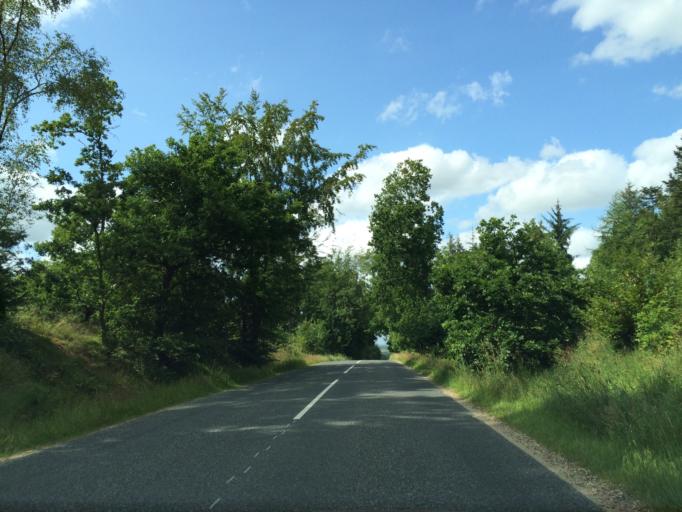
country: DK
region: Central Jutland
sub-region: Skanderborg Kommune
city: Ry
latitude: 56.1995
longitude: 9.7577
